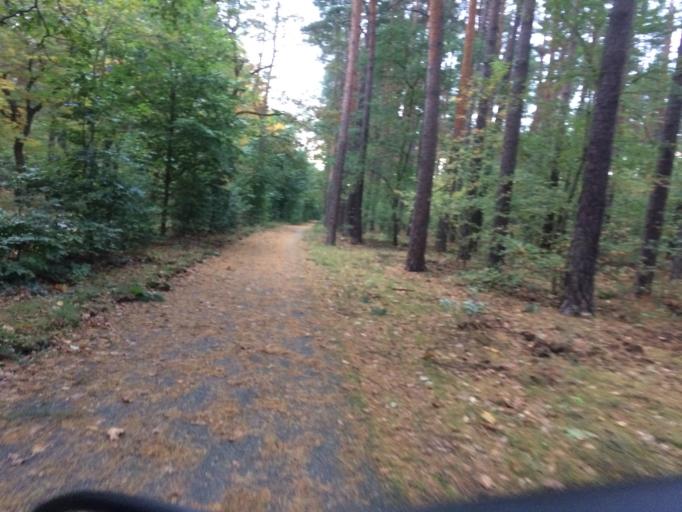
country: DE
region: Brandenburg
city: Birkenwerder
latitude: 52.7123
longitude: 13.2858
